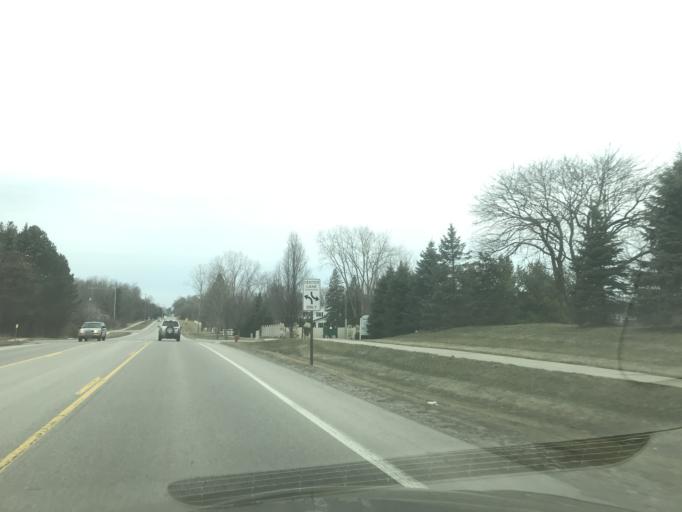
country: US
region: Michigan
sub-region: Ingham County
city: Haslett
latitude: 42.7554
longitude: -84.4283
